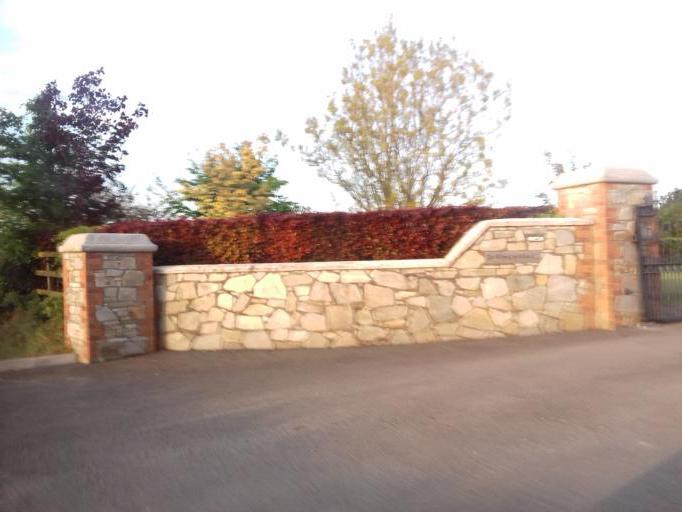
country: IE
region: Leinster
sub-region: Fingal County
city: Swords
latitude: 53.4927
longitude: -6.2141
